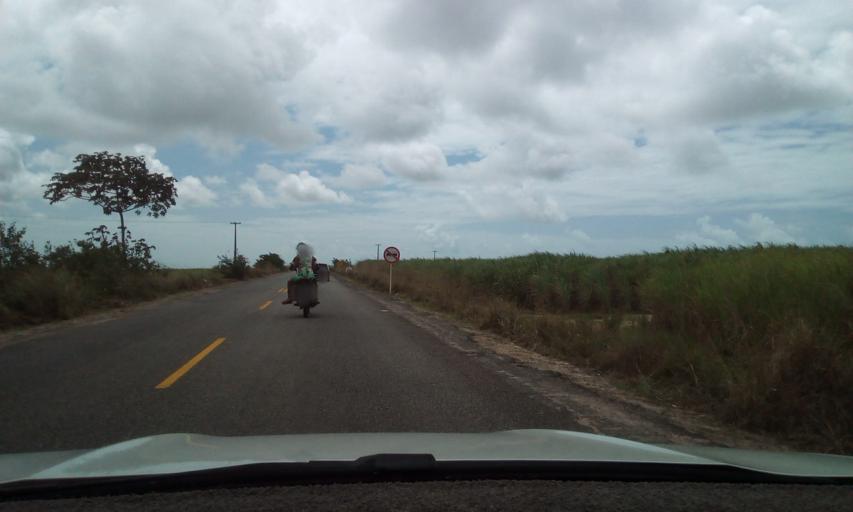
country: BR
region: Paraiba
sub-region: Rio Tinto
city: Rio Tinto
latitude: -6.7626
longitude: -35.0007
